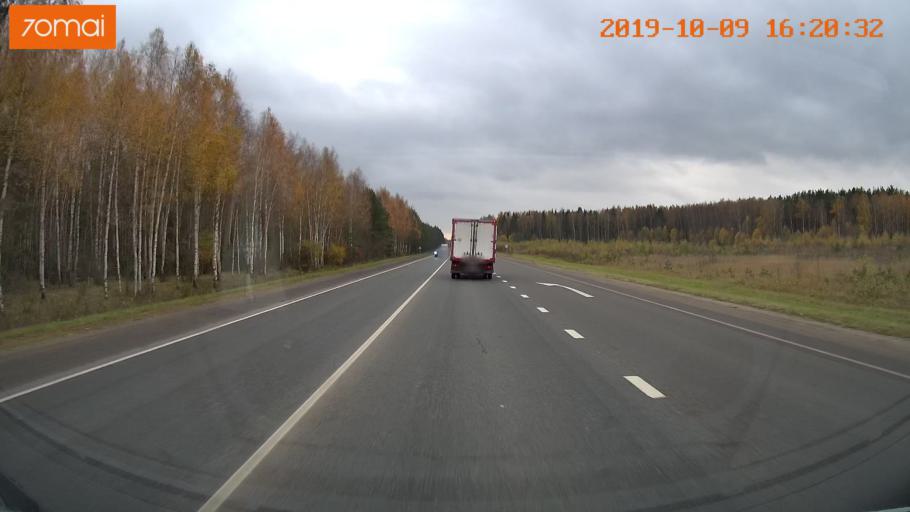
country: RU
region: Kostroma
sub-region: Kostromskoy Rayon
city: Kostroma
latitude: 57.7054
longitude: 40.8919
